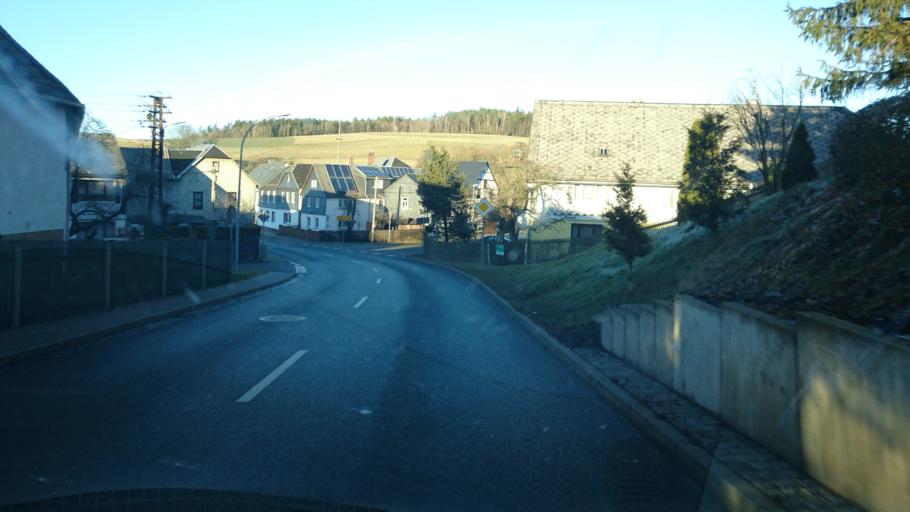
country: DE
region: Thuringia
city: Kirschkau
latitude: 50.6171
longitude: 11.9214
